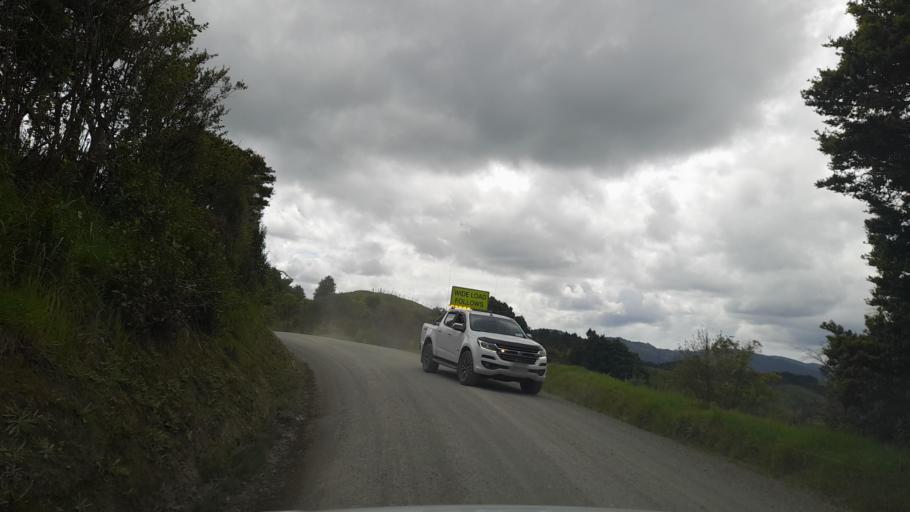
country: NZ
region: Auckland
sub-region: Auckland
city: Wellsford
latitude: -36.1633
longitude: 174.3544
